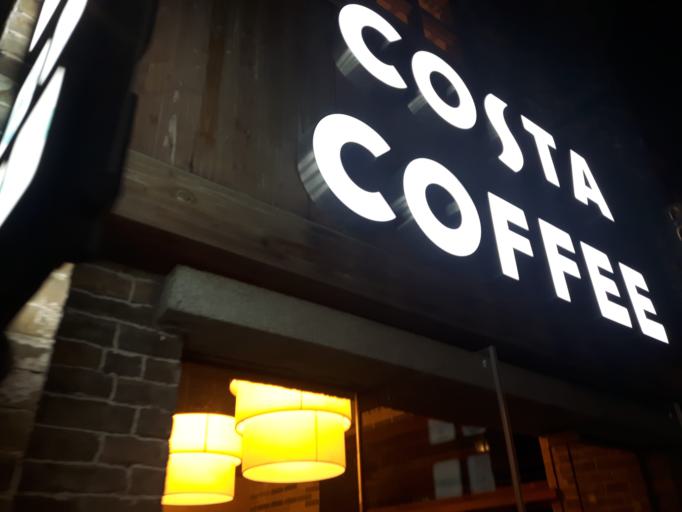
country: CN
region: Guangdong
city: Zumiao
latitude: 23.0324
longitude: 113.1104
